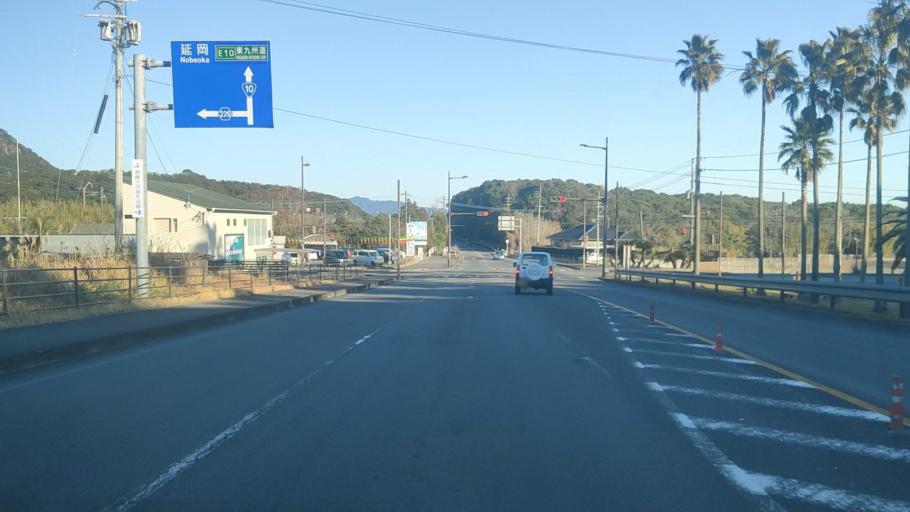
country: JP
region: Miyazaki
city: Nobeoka
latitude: 32.3789
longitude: 131.6276
